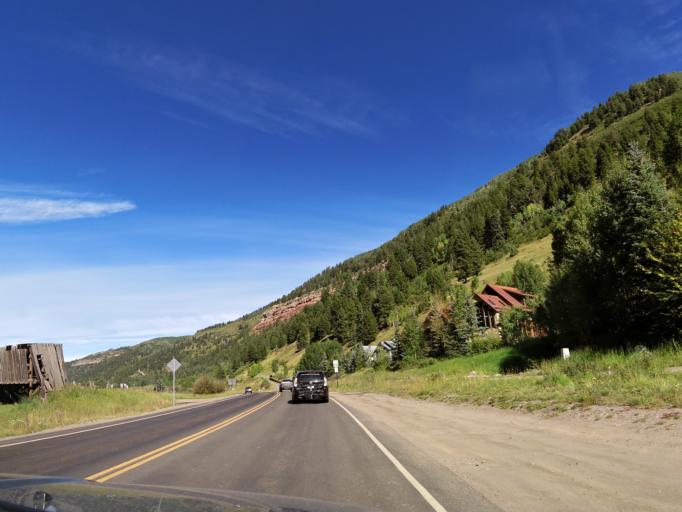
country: US
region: Colorado
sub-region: San Miguel County
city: Telluride
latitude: 37.9417
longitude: -107.8215
